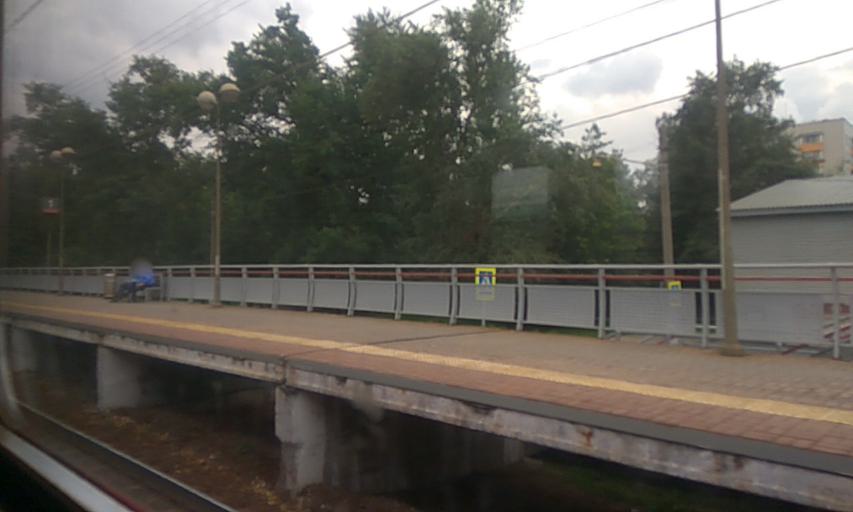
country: RU
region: Moscow
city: Ryazanskiy
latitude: 55.7315
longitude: 37.7728
